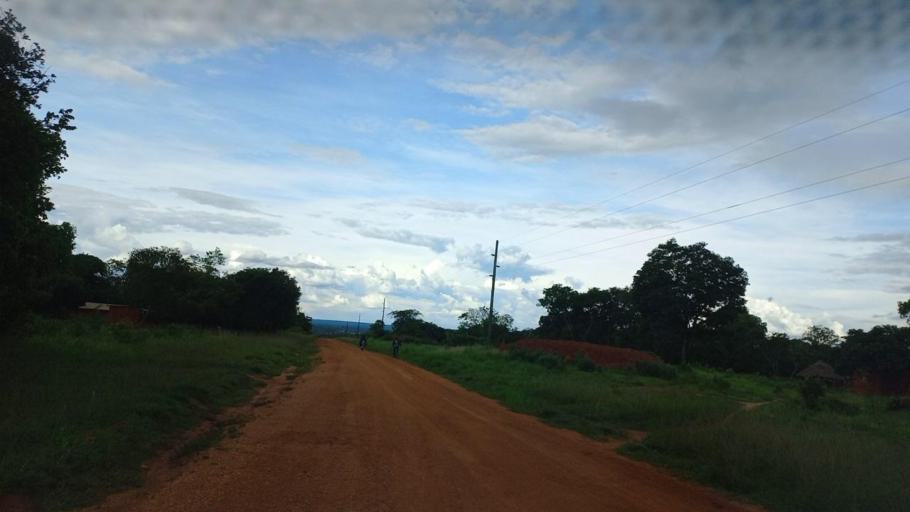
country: ZM
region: North-Western
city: Mwinilunga
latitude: -11.7662
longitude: 24.4115
